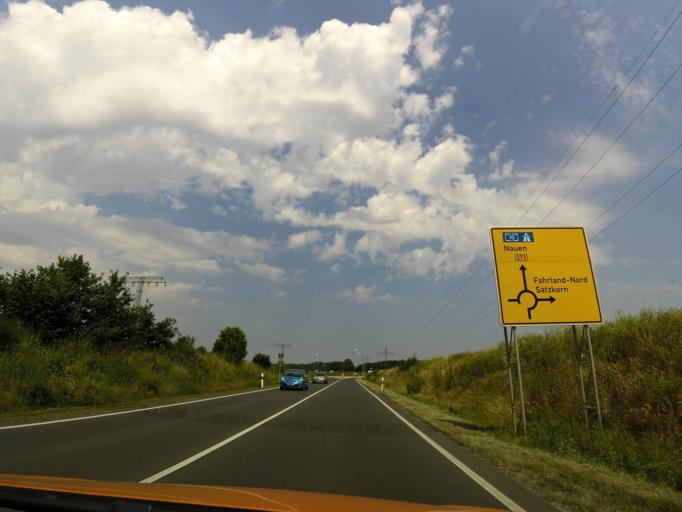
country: DE
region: Brandenburg
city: Werder
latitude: 52.4610
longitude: 12.9746
